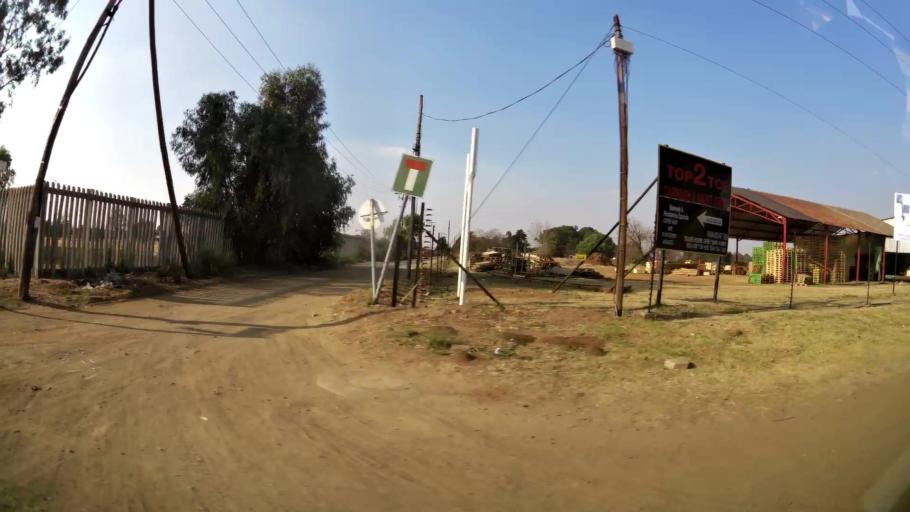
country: ZA
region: Gauteng
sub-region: Ekurhuleni Metropolitan Municipality
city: Benoni
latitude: -26.1193
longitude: 28.3783
